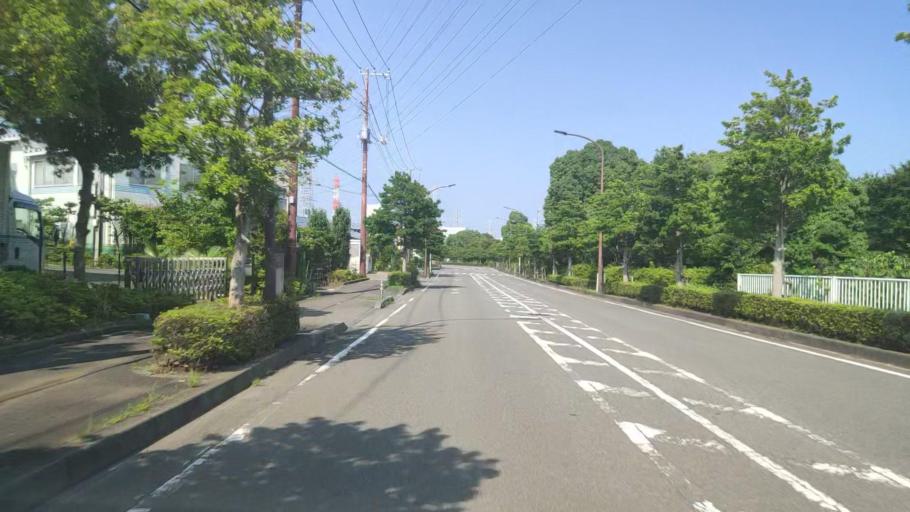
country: JP
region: Kanagawa
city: Hiratsuka
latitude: 35.3566
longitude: 139.3378
